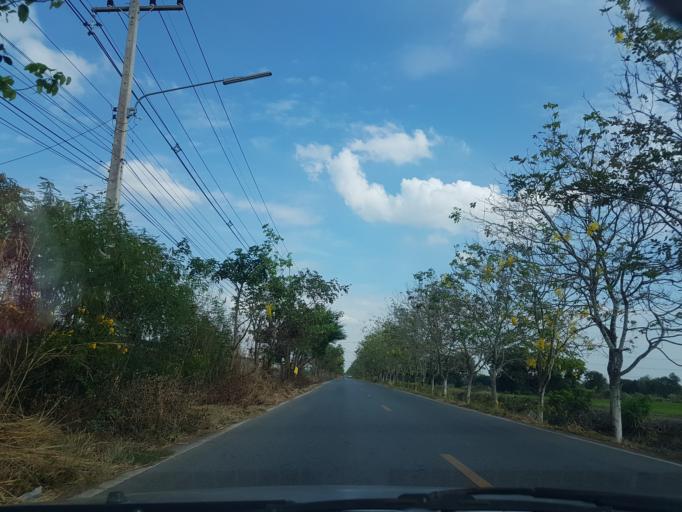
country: TH
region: Pathum Thani
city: Nong Suea
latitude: 14.1358
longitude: 100.8745
